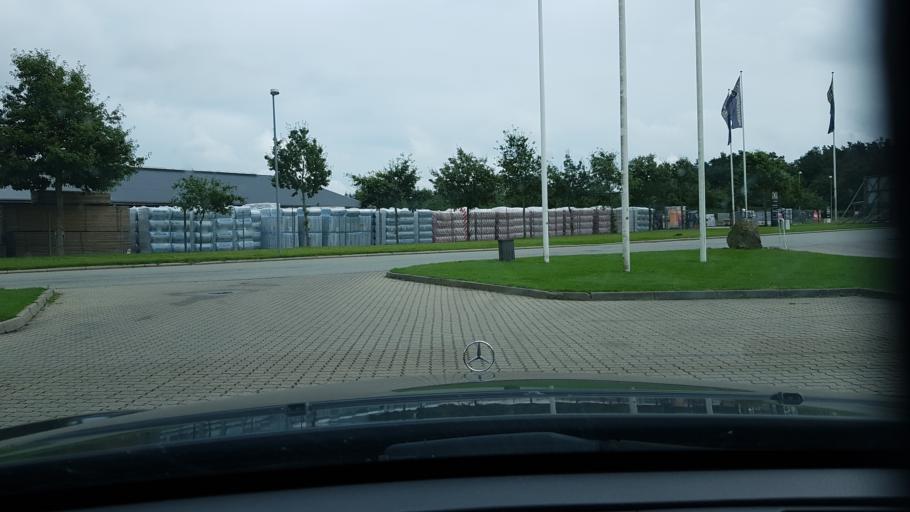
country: DK
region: North Denmark
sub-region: Mariagerfjord Kommune
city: Hadsund
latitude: 56.7286
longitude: 10.1358
